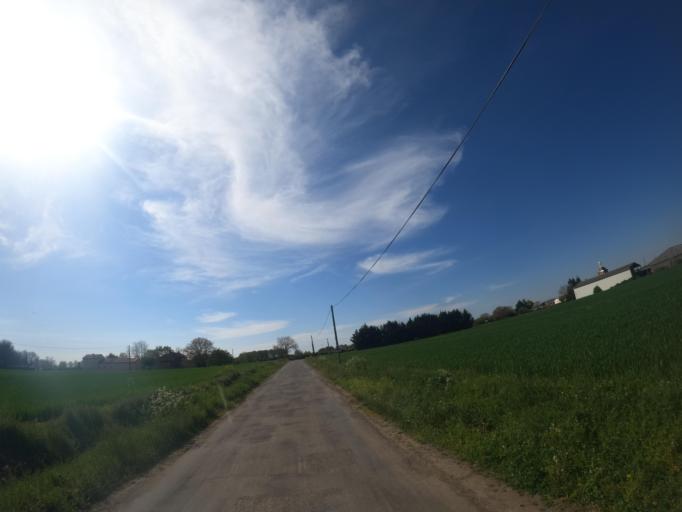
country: FR
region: Poitou-Charentes
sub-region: Departement des Deux-Sevres
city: Saint-Varent
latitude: 46.9125
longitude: -0.2153
